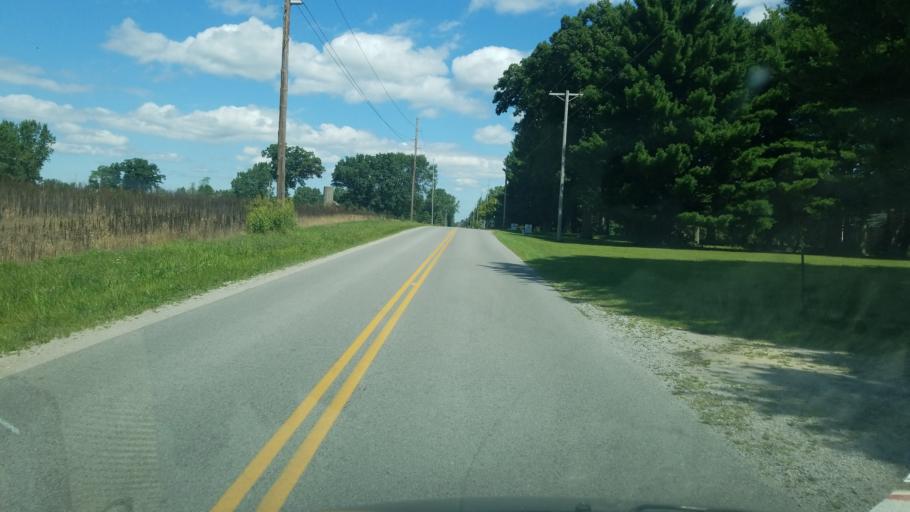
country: US
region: Ohio
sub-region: Henry County
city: Liberty Center
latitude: 41.4562
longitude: -83.9214
